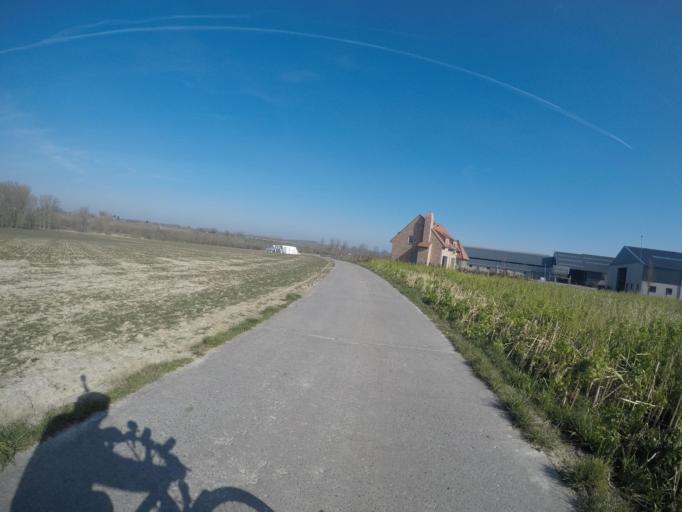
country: BE
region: Flanders
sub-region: Provincie Oost-Vlaanderen
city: Sint-Maria-Lierde
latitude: 50.7977
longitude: 3.8638
